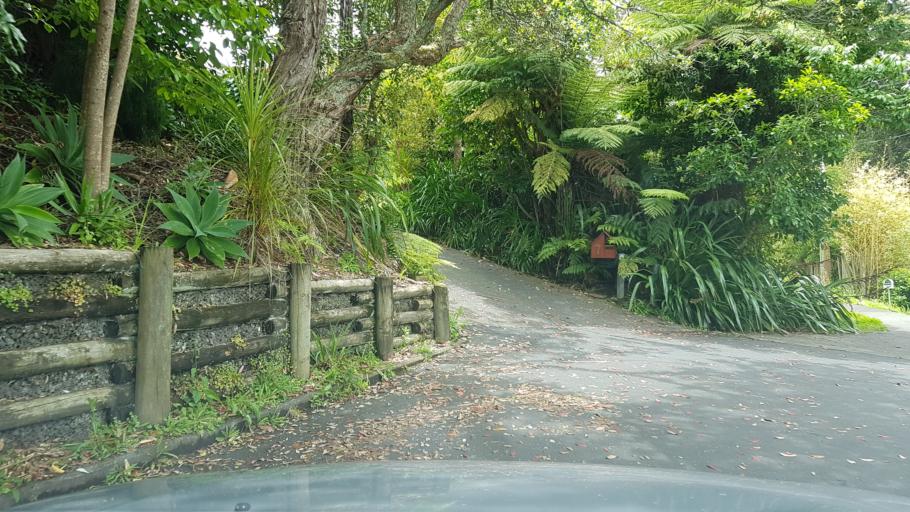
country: NZ
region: Auckland
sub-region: Auckland
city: North Shore
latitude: -36.8158
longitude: 174.7261
